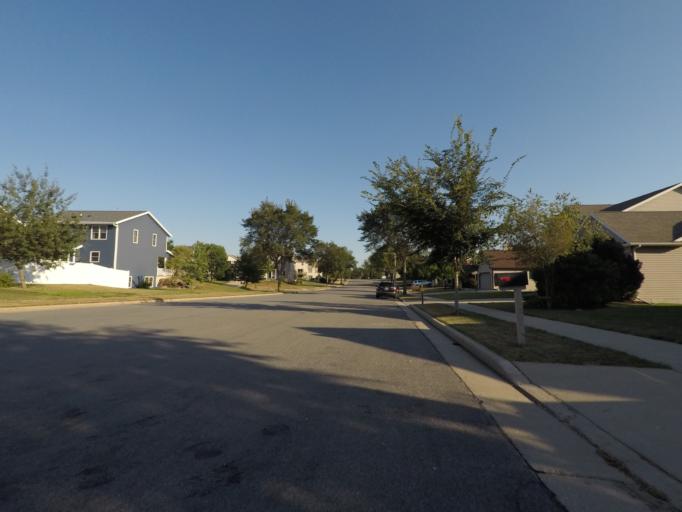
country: US
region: Wisconsin
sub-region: Dane County
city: Verona
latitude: 43.0054
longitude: -89.5422
